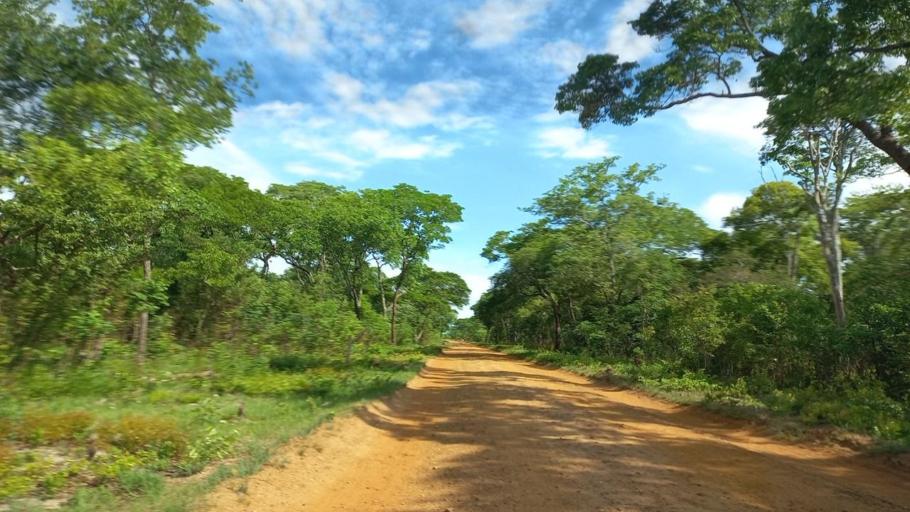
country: ZM
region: North-Western
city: Kabompo
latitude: -13.0809
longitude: 24.2196
